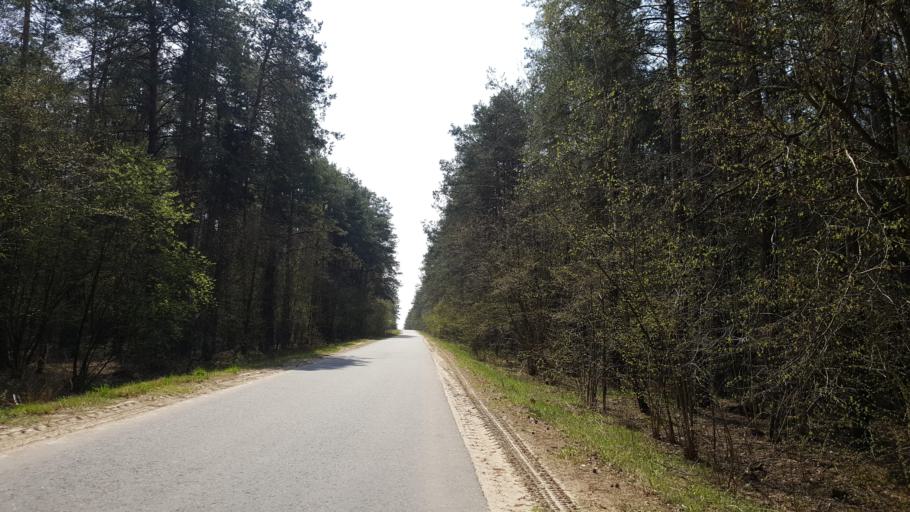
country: BY
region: Brest
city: Kamyanyets
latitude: 52.3406
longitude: 23.8223
